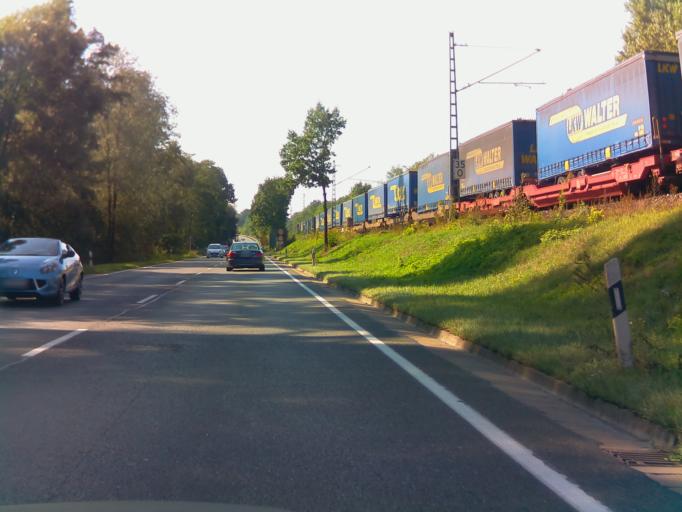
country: DE
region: Bavaria
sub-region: Upper Franconia
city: Michelau
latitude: 50.1531
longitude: 11.1020
